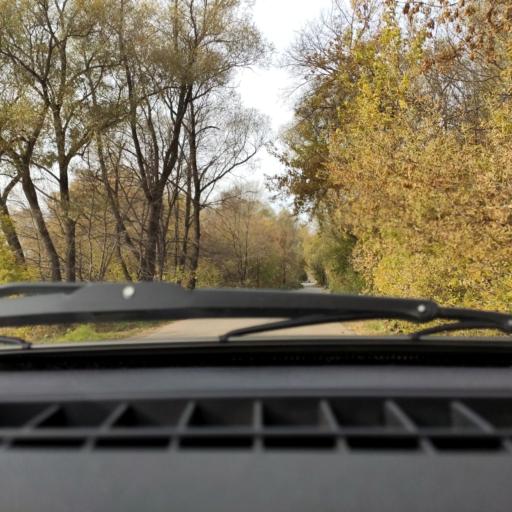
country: RU
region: Bashkortostan
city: Ufa
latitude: 54.7848
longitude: 56.1656
